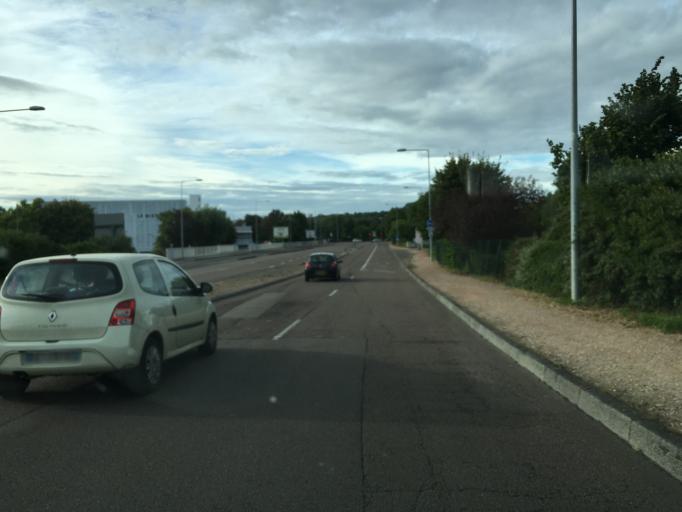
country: FR
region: Bourgogne
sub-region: Departement de la Cote-d'Or
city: Dijon
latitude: 47.3185
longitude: 5.0108
